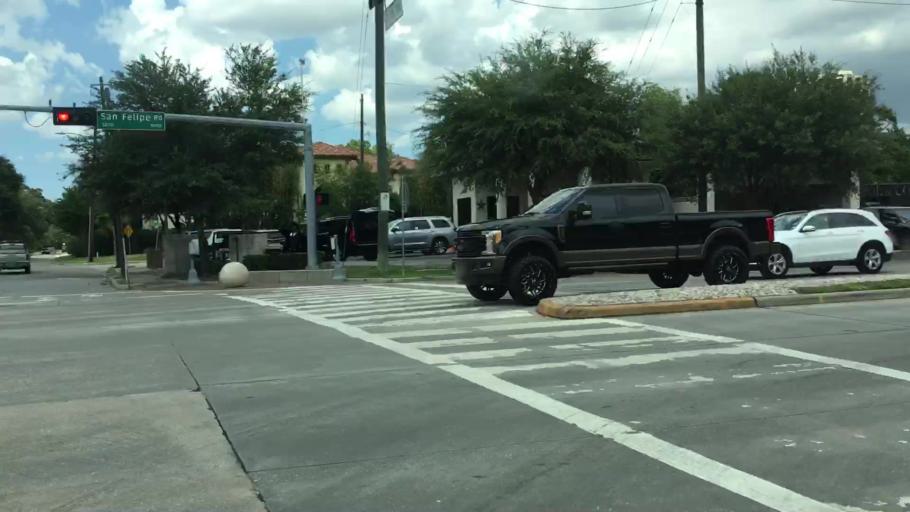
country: US
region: Texas
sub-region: Harris County
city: Hunters Creek Village
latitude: 29.7501
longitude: -95.4671
